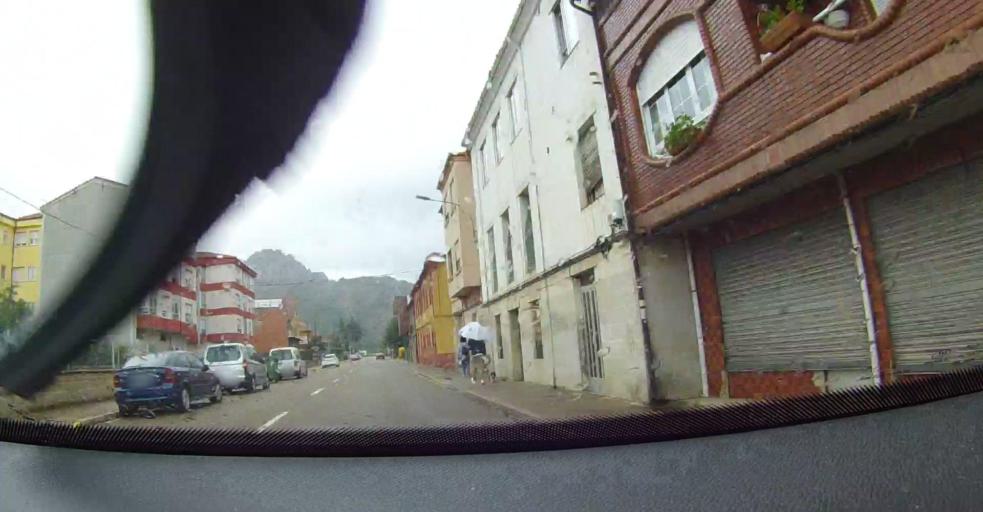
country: ES
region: Castille and Leon
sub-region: Provincia de Leon
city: Cistierna
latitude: 42.8066
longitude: -5.1295
